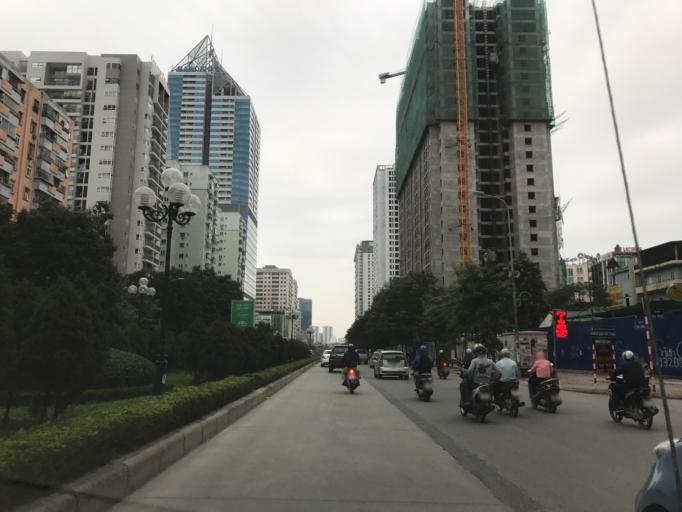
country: VN
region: Ha Noi
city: Thanh Xuan
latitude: 21.0033
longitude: 105.8019
